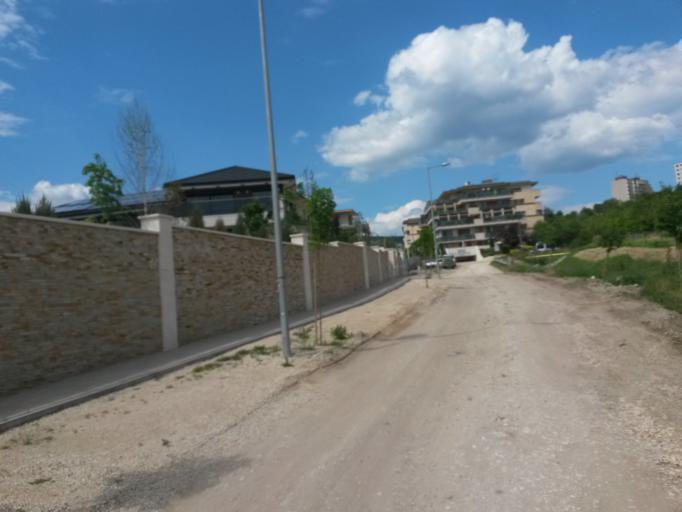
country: HU
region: Budapest
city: Budapest XII. keruelet
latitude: 47.4670
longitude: 18.9933
